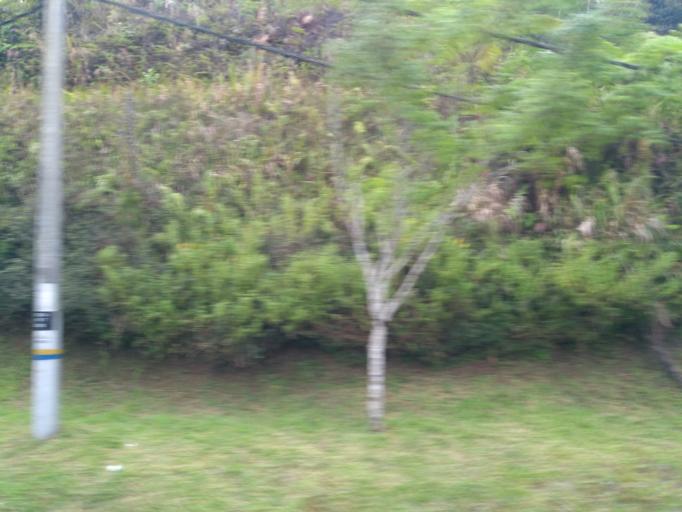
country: MY
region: Pahang
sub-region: Cameron Highlands
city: Tanah Rata
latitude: 4.5083
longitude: 101.4128
